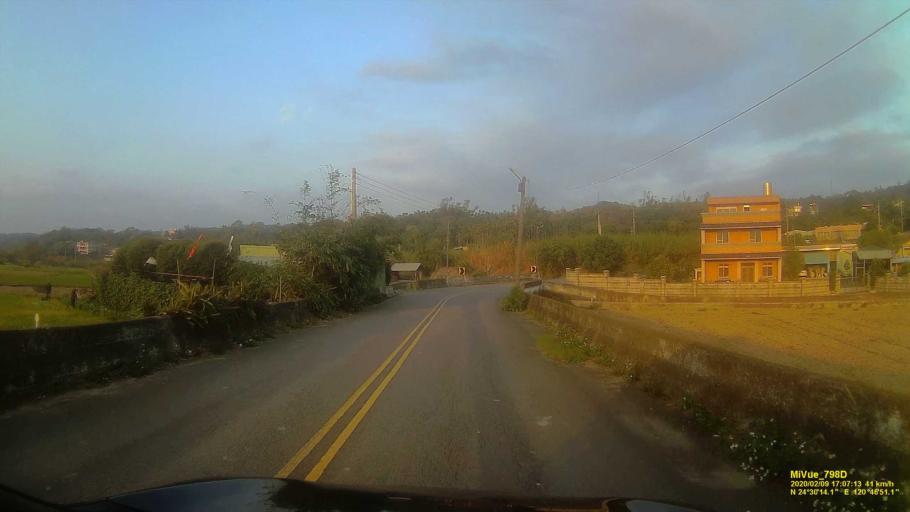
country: TW
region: Taiwan
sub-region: Miaoli
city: Miaoli
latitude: 24.5041
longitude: 120.7809
